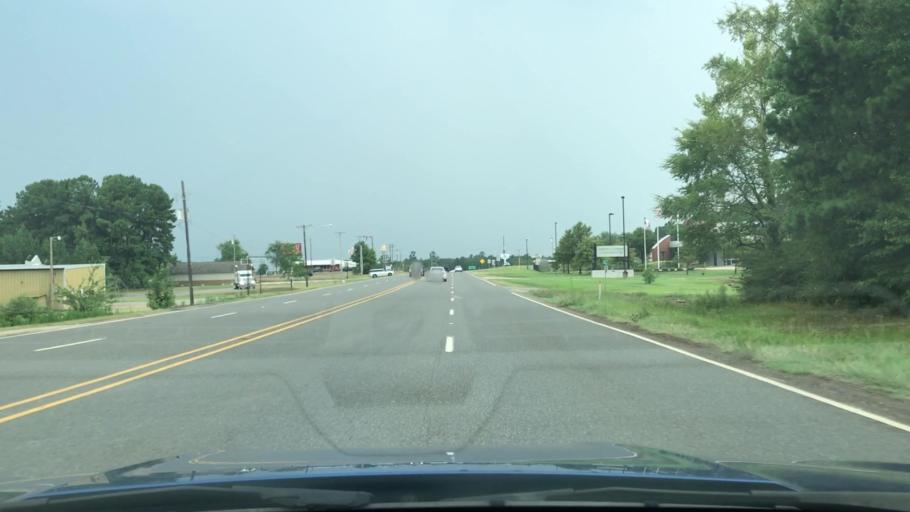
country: US
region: Texas
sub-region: Harrison County
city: Waskom
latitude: 32.4728
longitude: -94.0540
